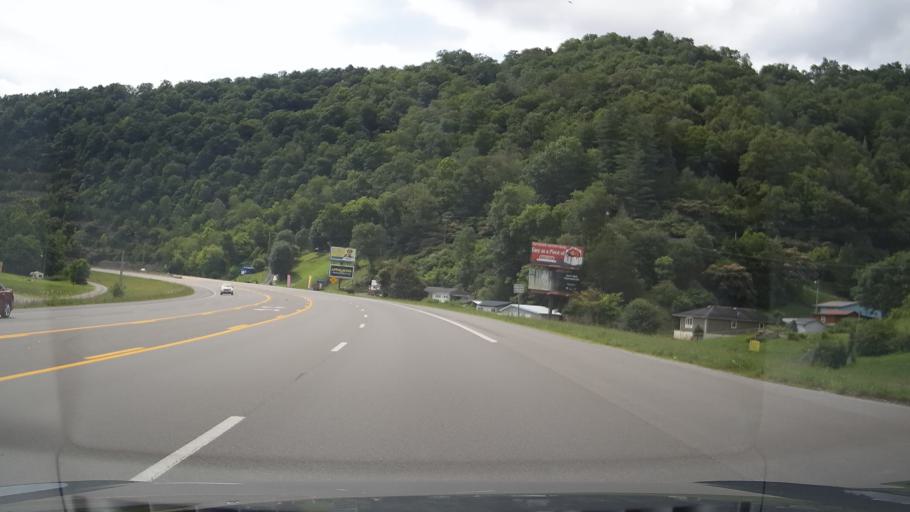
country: US
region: Kentucky
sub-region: Pike County
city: Coal Run Village
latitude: 37.5418
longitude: -82.5835
